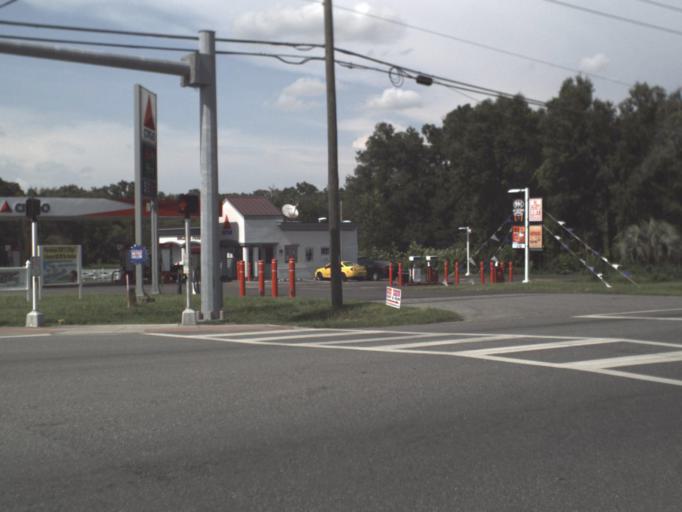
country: US
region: Florida
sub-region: Citrus County
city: Citrus Springs
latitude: 28.9657
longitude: -82.4186
